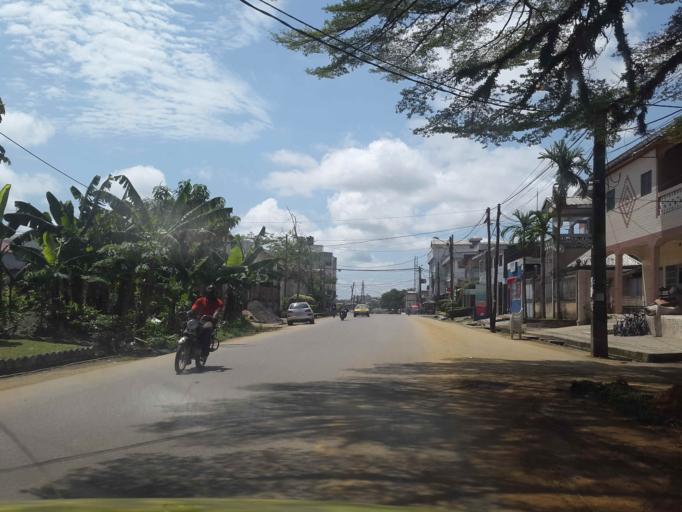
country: CM
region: Littoral
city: Douala
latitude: 4.0871
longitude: 9.7428
